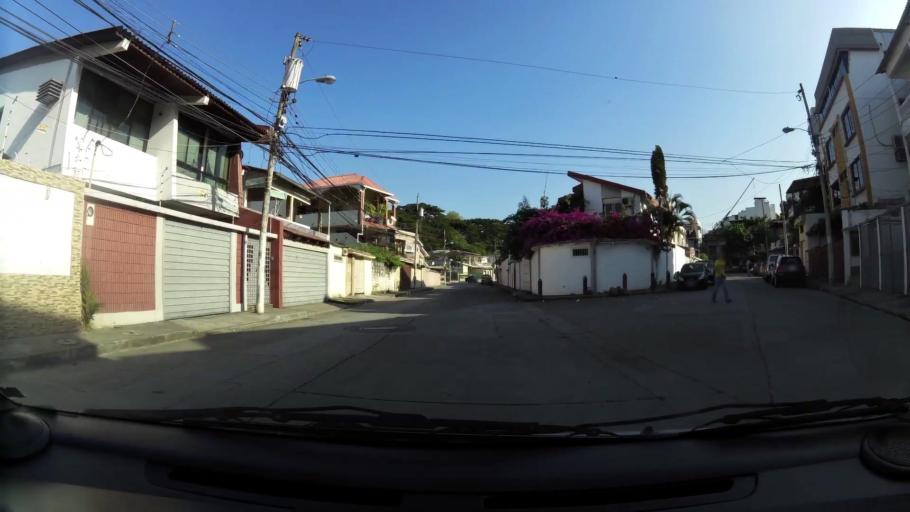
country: EC
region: Guayas
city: Guayaquil
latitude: -2.1584
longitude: -79.9072
